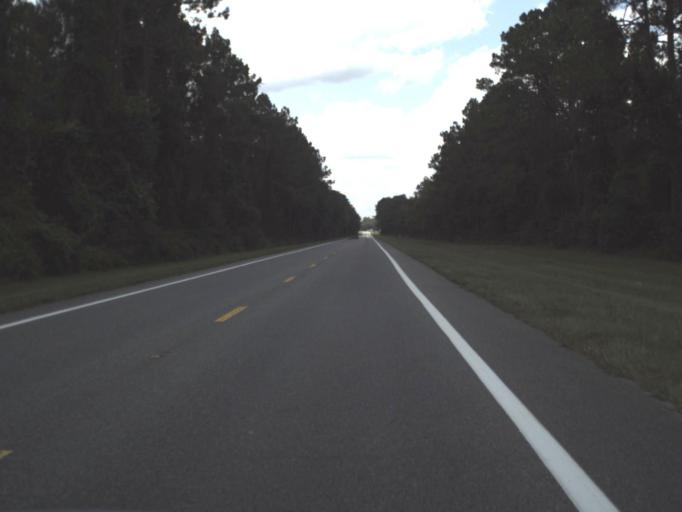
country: US
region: Florida
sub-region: Union County
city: Lake Butler
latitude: 30.0863
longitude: -82.2160
